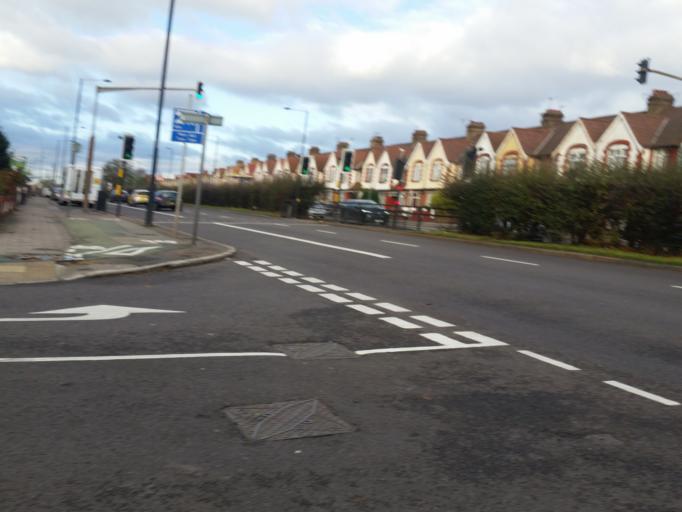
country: GB
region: England
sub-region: Greater London
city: Harringay
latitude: 51.6071
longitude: -0.0859
